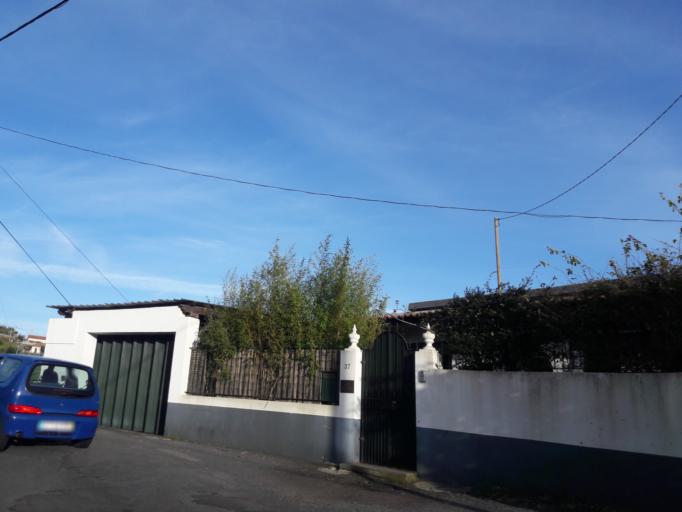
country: PT
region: Madeira
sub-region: Santa Cruz
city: Camacha
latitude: 32.6655
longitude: -16.8458
